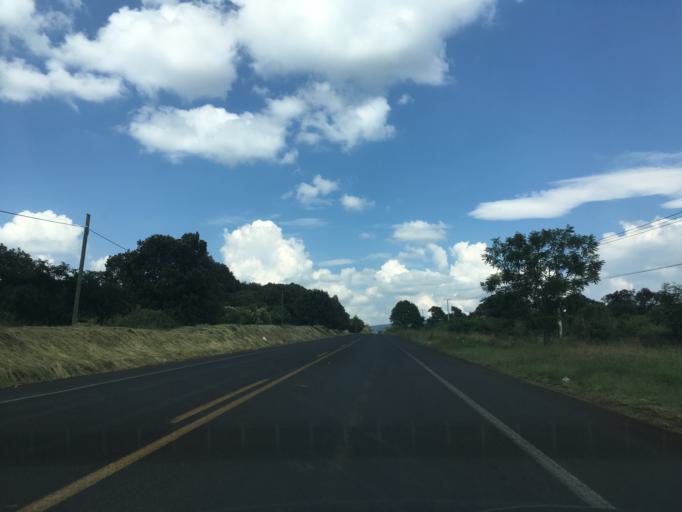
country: MX
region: Michoacan
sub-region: Tingueindin
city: Tingueindin
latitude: 19.8178
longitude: -102.5115
